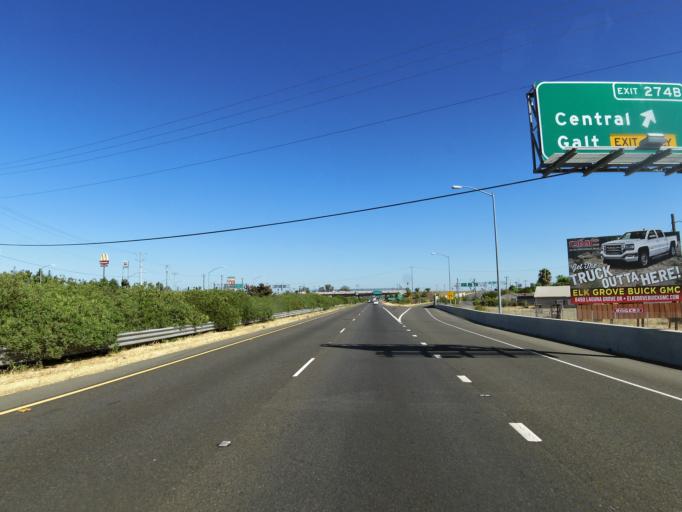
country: US
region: California
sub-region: Sacramento County
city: Galt
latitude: 38.2515
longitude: -121.2916
